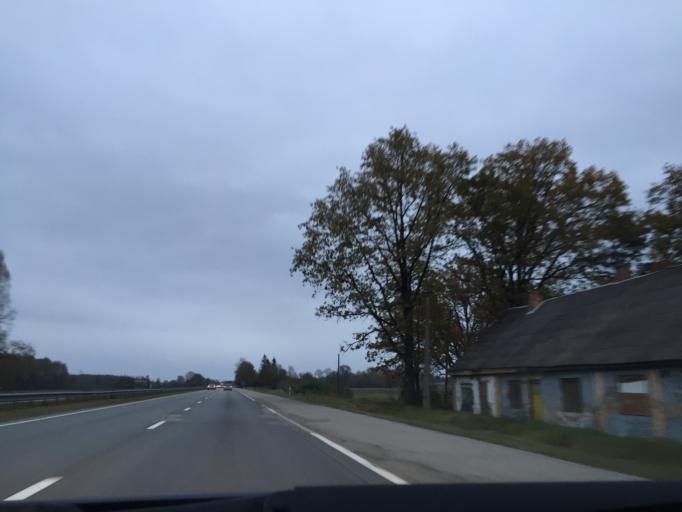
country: LV
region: Olaine
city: Olaine
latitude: 56.7603
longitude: 23.9086
